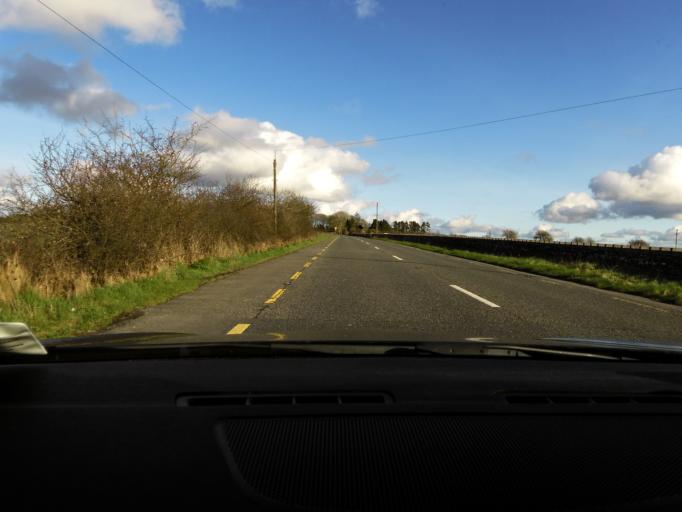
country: IE
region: Connaught
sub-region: Roscommon
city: Castlerea
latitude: 53.6805
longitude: -8.3524
